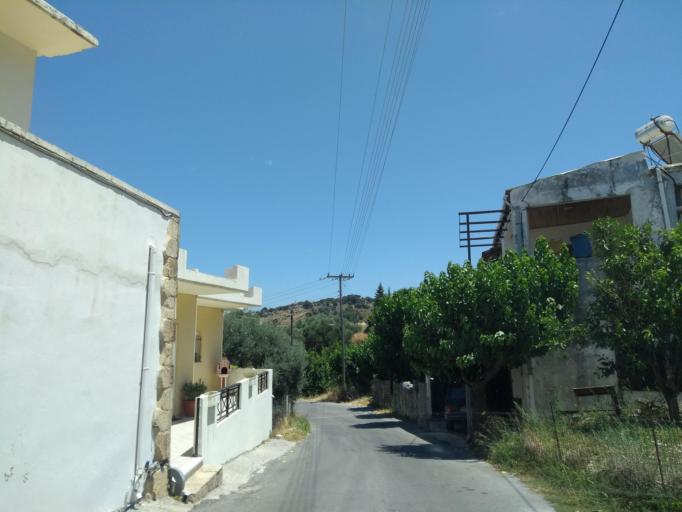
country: GR
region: Crete
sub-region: Nomos Chanias
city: Georgioupolis
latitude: 35.3146
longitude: 24.2994
